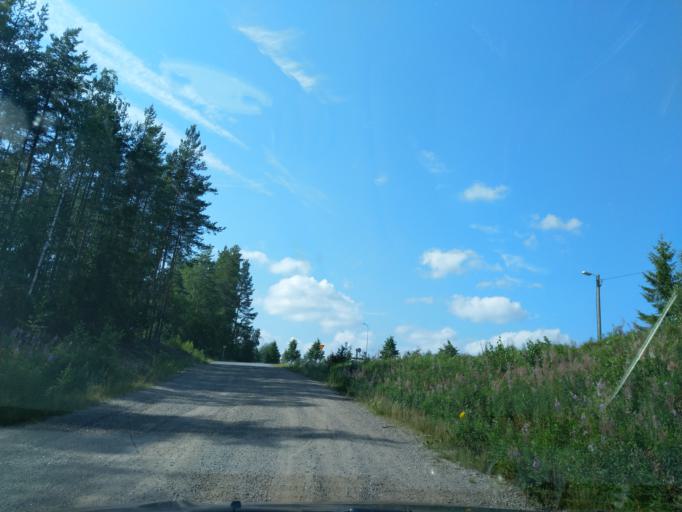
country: FI
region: South Karelia
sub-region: Lappeenranta
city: Lappeenranta
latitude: 61.0368
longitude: 28.1239
